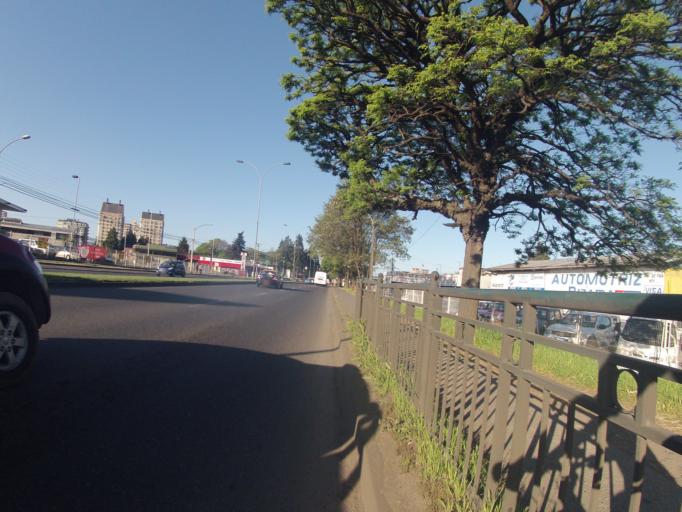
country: CL
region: Araucania
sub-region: Provincia de Cautin
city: Temuco
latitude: -38.7425
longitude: -72.6050
